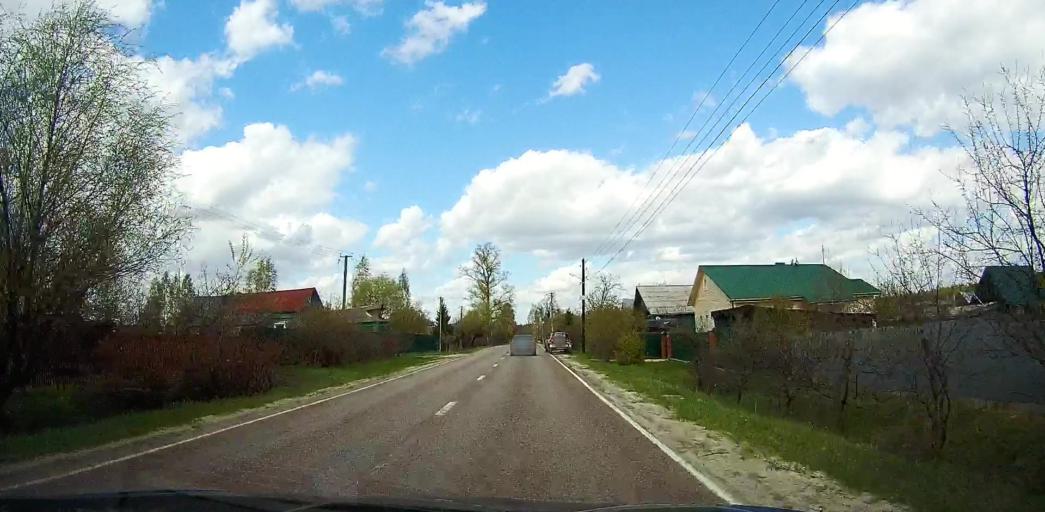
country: RU
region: Moskovskaya
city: Davydovo
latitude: 55.5834
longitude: 38.8267
